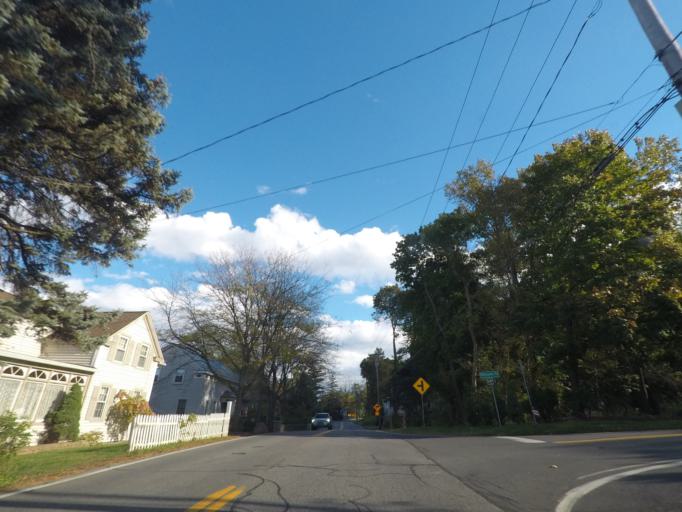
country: US
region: New York
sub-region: Schenectady County
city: Niskayuna
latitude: 42.7765
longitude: -73.8242
